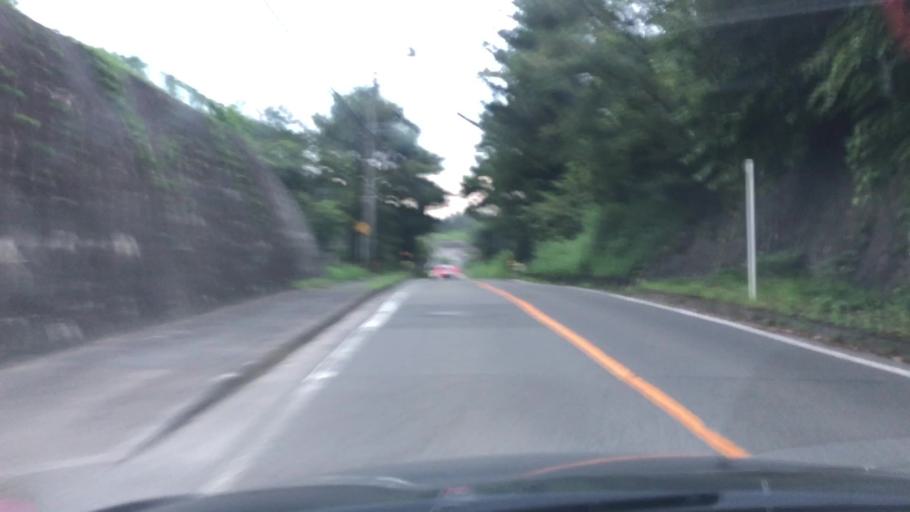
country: JP
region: Tokyo
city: Ome
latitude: 35.7555
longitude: 139.2365
